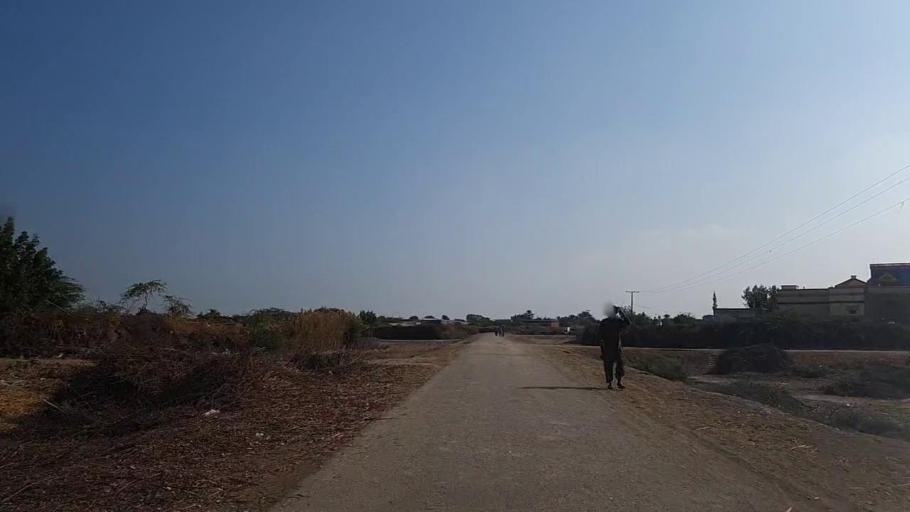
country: PK
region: Sindh
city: Jam Sahib
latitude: 26.2766
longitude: 68.5830
